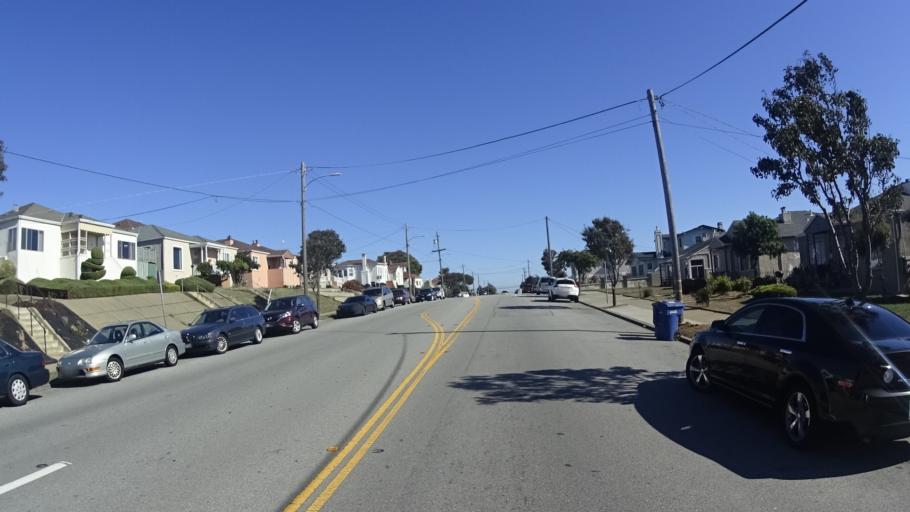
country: US
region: California
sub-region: San Mateo County
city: South San Francisco
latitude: 37.6595
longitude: -122.4296
